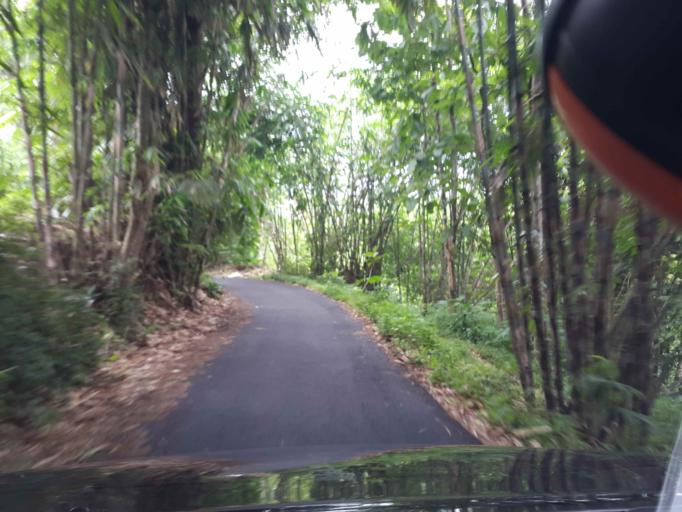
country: ID
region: Central Java
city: Salatiga
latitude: -7.3391
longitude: 110.5165
